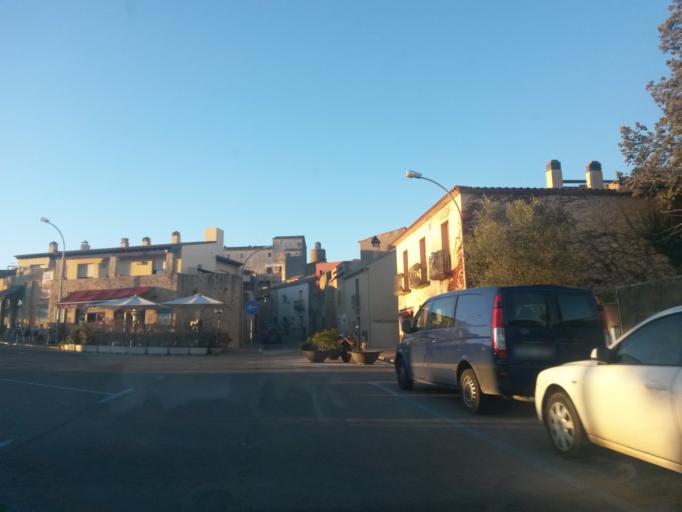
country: ES
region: Catalonia
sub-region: Provincia de Girona
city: Pals
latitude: 41.9700
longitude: 3.1464
